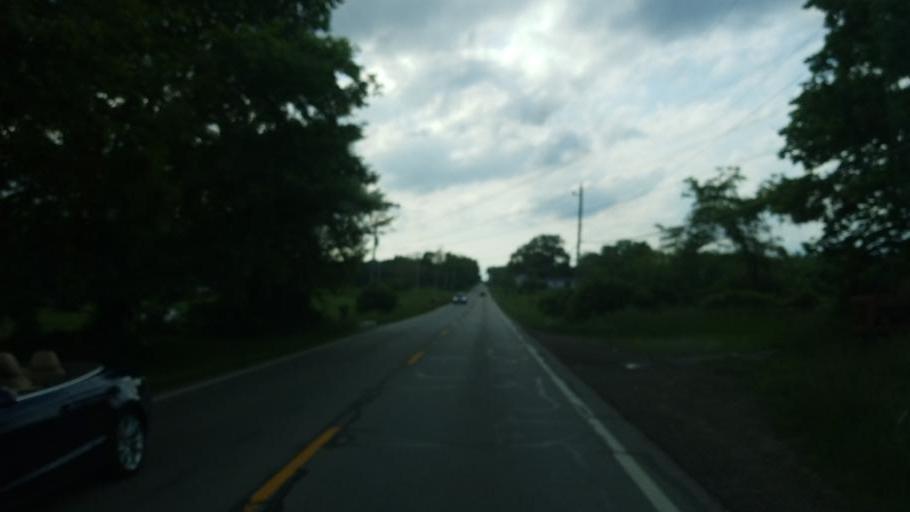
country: US
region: Ohio
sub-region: Delaware County
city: Sunbury
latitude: 40.2207
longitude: -82.8090
